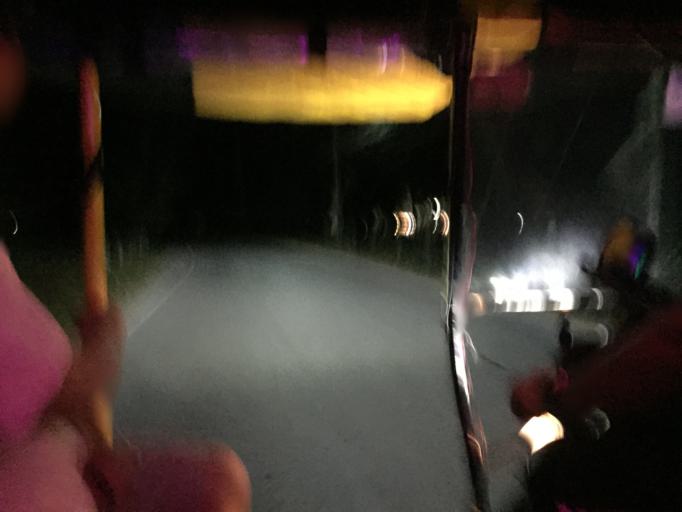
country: TH
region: Phuket
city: Thalang
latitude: 7.9868
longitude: 98.2922
